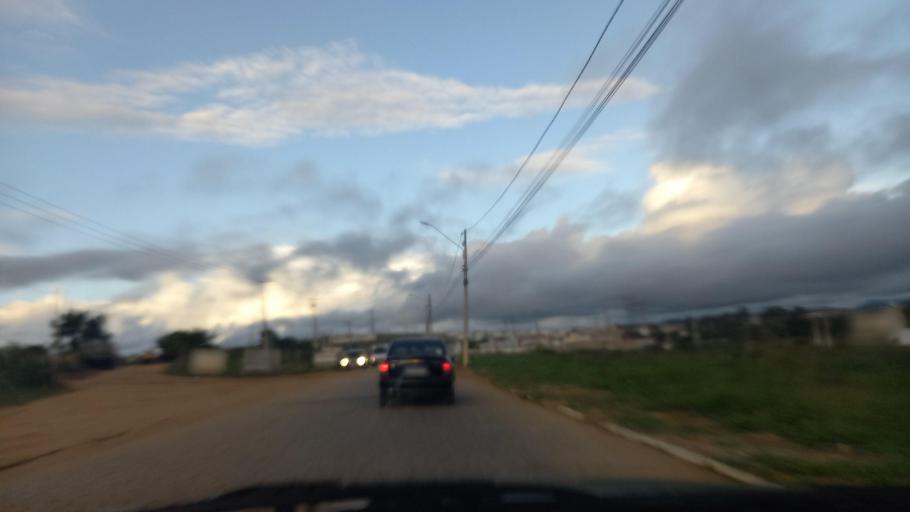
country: BR
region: Pernambuco
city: Garanhuns
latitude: -8.8907
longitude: -36.4486
